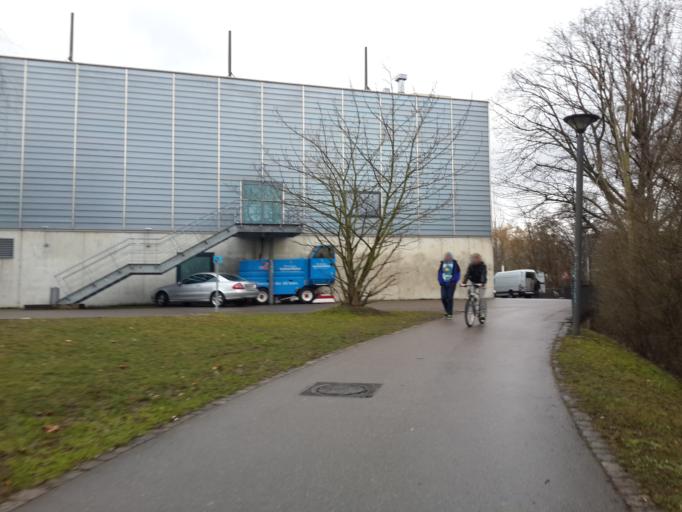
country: DE
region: Baden-Wuerttemberg
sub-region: Regierungsbezirk Stuttgart
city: Heilbronn
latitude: 49.1460
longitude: 9.2144
